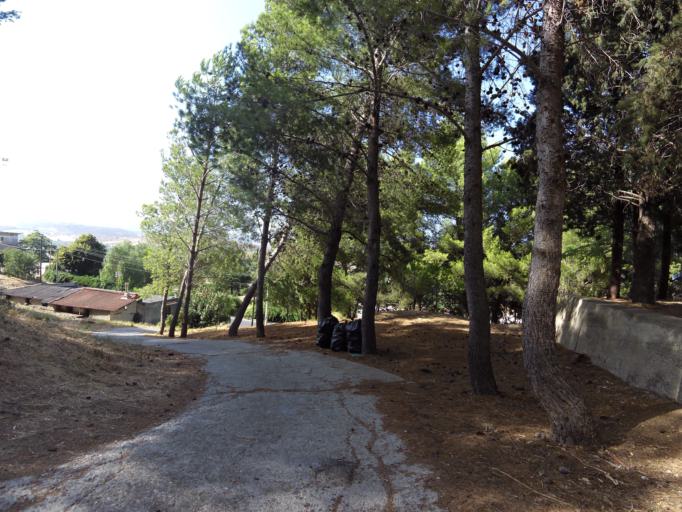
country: IT
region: Calabria
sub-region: Provincia di Reggio Calabria
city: Monasterace
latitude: 38.4539
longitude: 16.5541
